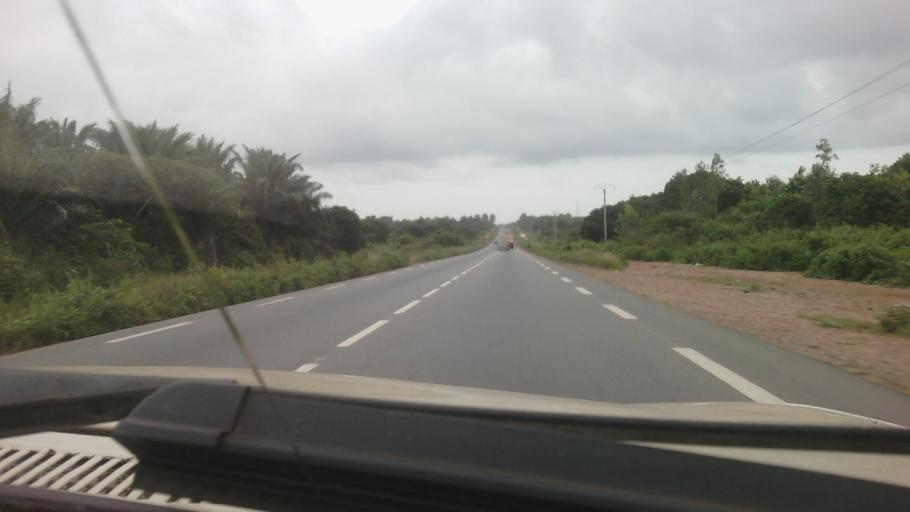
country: BJ
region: Atlantique
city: Ouidah
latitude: 6.3827
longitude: 2.0190
